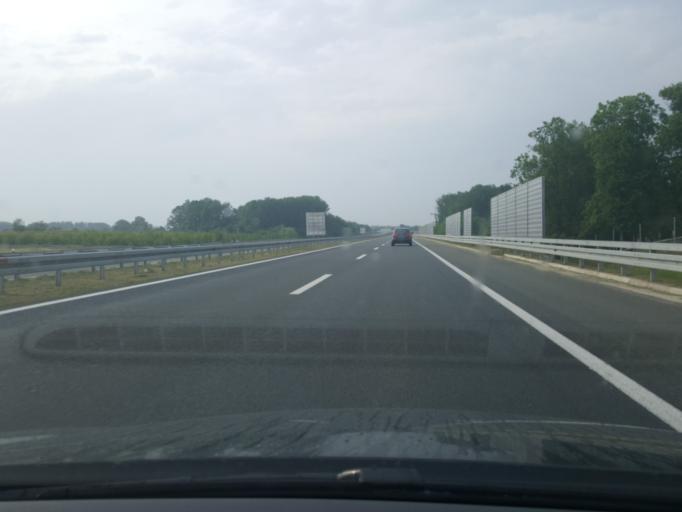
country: RS
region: Central Serbia
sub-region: Kolubarski Okrug
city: Lajkovac
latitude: 44.3692
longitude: 20.1193
